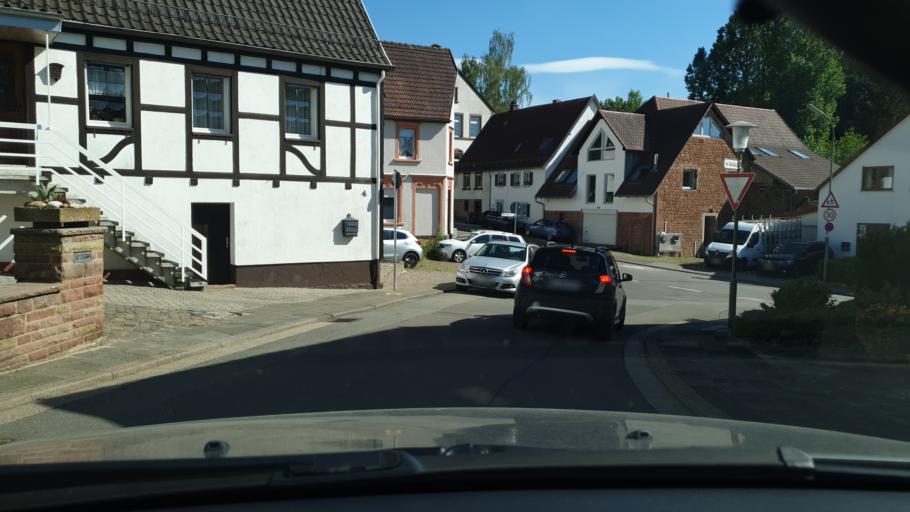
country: DE
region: Rheinland-Pfalz
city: Otterbach
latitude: 49.4802
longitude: 7.7718
